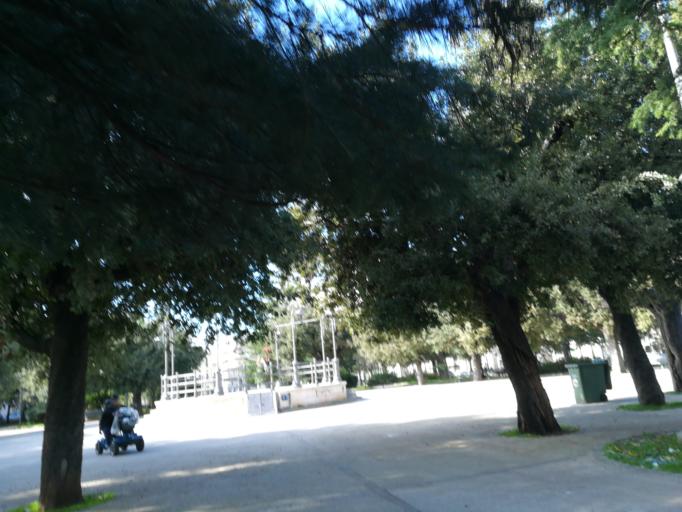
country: IT
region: Apulia
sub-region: Provincia di Bari
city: Bitonto
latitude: 41.1120
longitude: 16.6960
